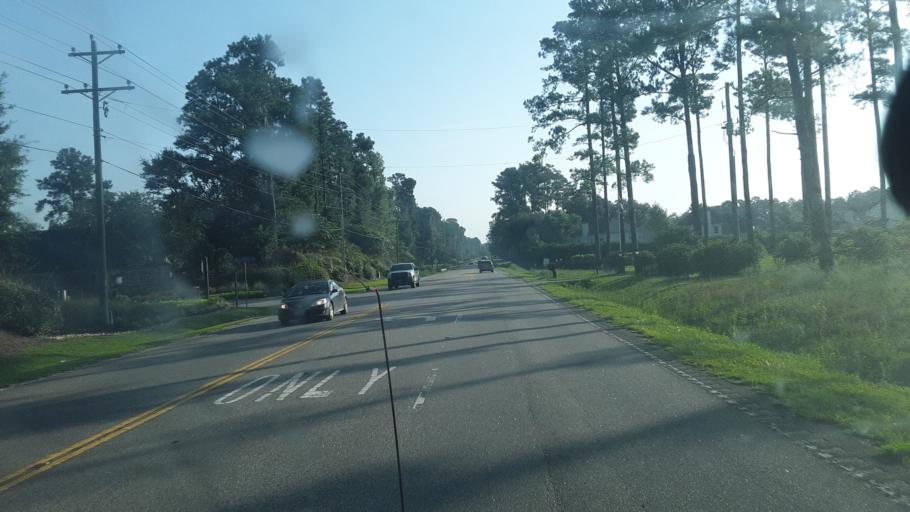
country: US
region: South Carolina
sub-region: Horry County
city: Forestbrook
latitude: 33.8233
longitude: -78.9009
